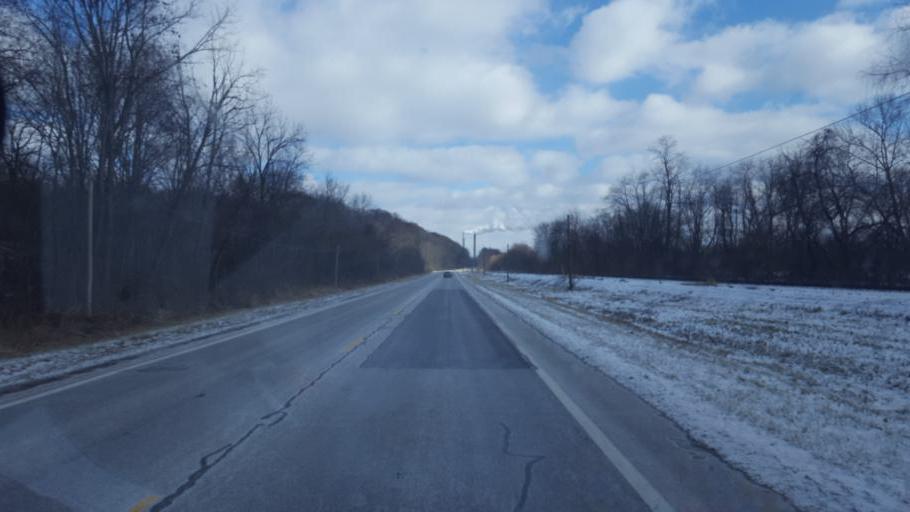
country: US
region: Ohio
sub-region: Muskingum County
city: Dresden
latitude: 40.1638
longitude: -81.9246
